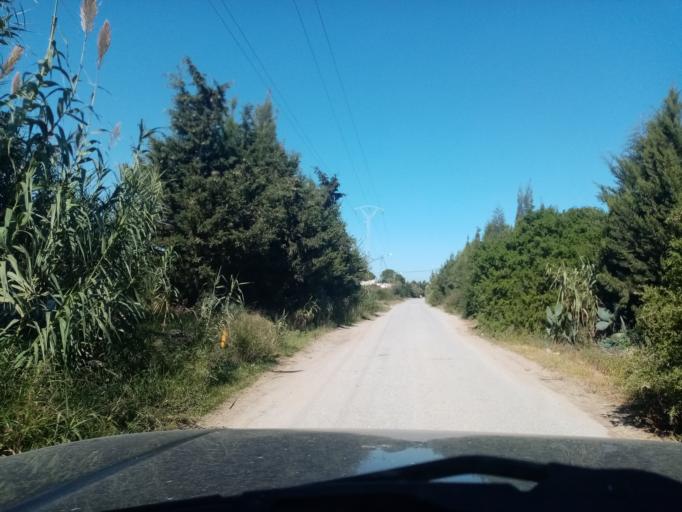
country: TN
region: Nabul
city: Bu `Urqub
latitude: 36.5707
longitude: 10.5761
